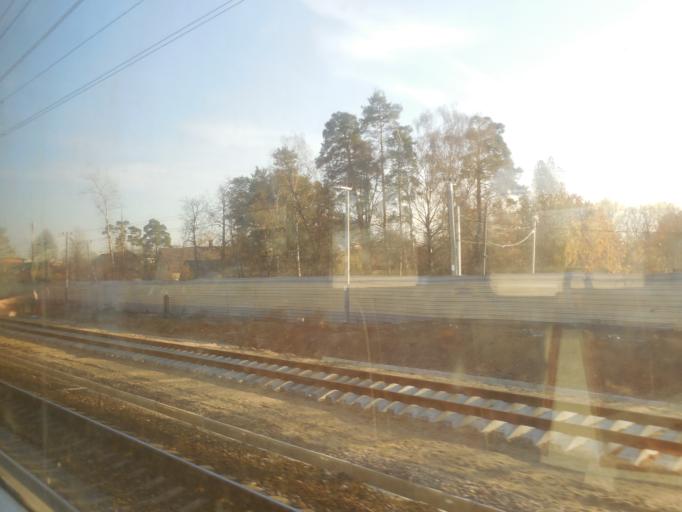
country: RU
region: Moskovskaya
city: Saltykovka
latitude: 55.7586
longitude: 37.9178
